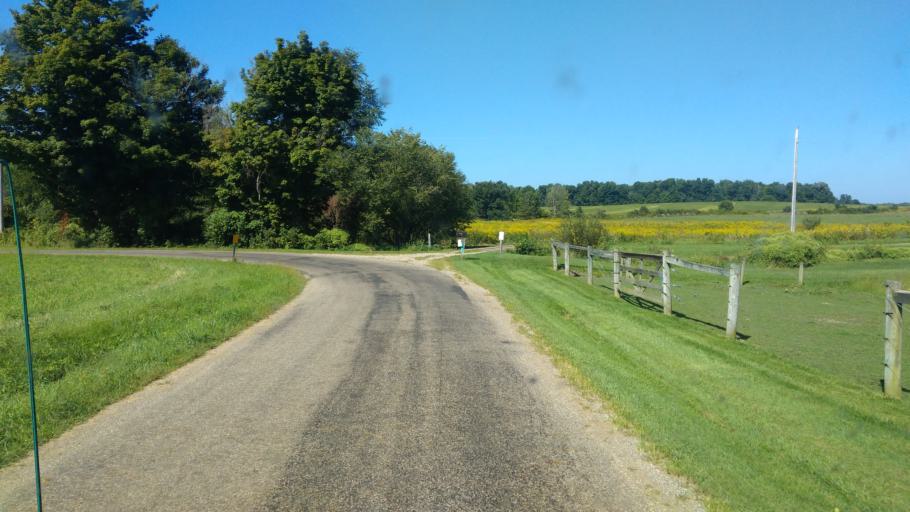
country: US
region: Ohio
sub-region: Knox County
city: Fredericktown
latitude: 40.4504
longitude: -82.4947
